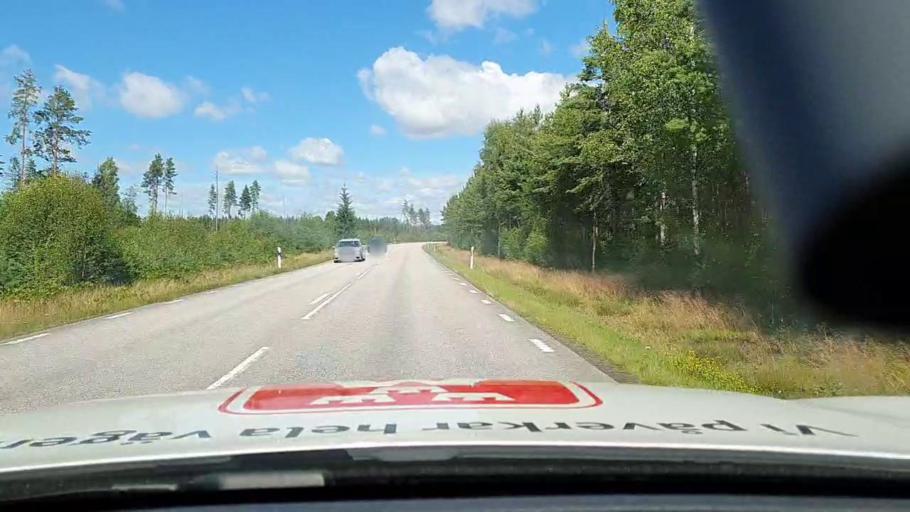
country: SE
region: Vaestra Goetaland
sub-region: Skovde Kommun
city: Stopen
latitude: 58.4414
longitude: 13.9361
